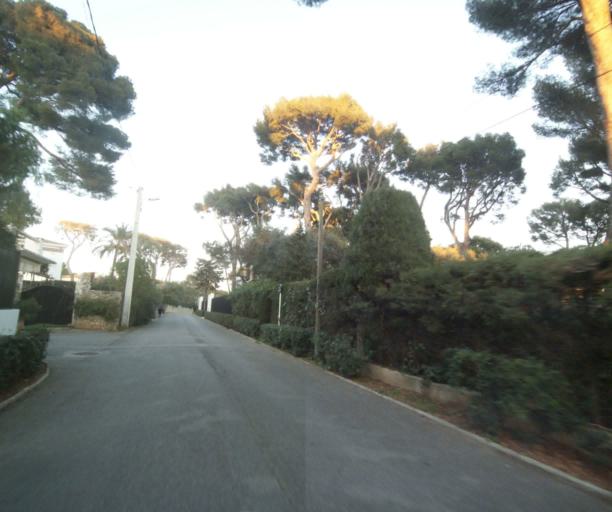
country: FR
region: Provence-Alpes-Cote d'Azur
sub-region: Departement des Alpes-Maritimes
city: Antibes
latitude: 43.5602
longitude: 7.1333
